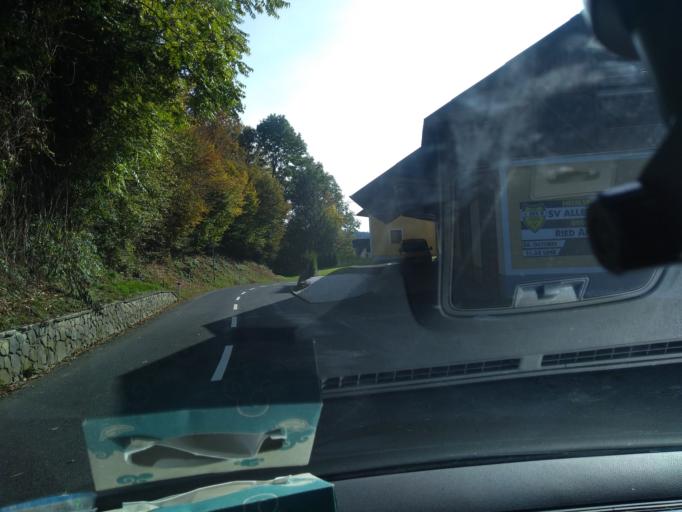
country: AT
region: Styria
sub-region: Politischer Bezirk Leibnitz
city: Sankt Ulrich am Waasen
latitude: 46.9218
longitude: 15.5317
